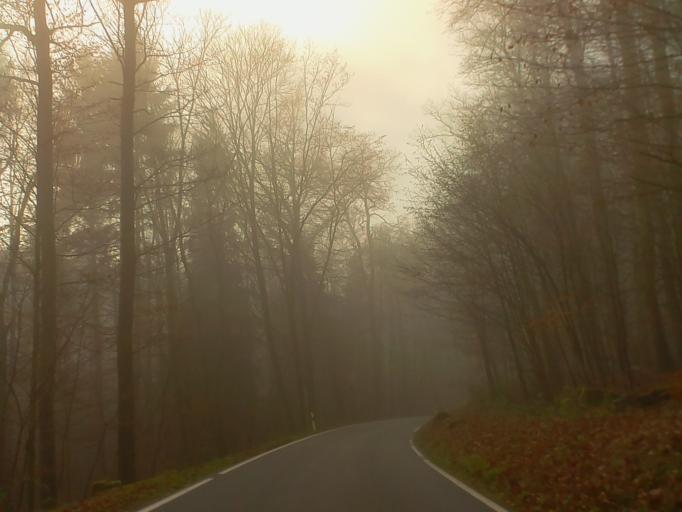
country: DE
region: Baden-Wuerttemberg
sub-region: Karlsruhe Region
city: Heddesbach
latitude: 49.4963
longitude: 8.8383
